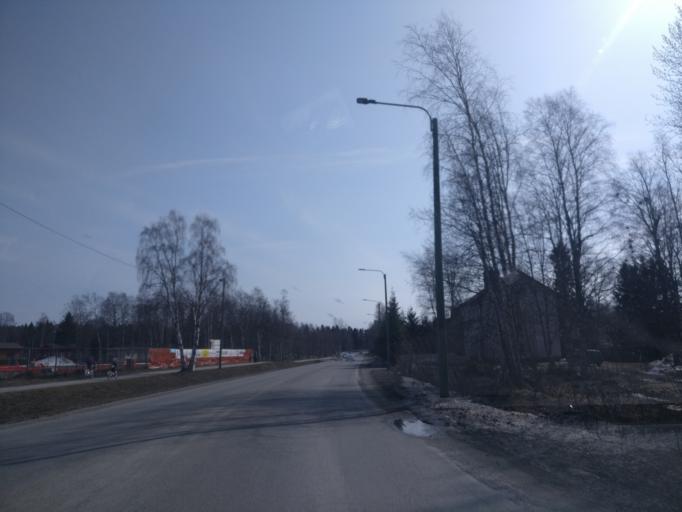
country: FI
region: Lapland
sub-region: Kemi-Tornio
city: Kemi
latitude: 65.7276
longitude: 24.6136
